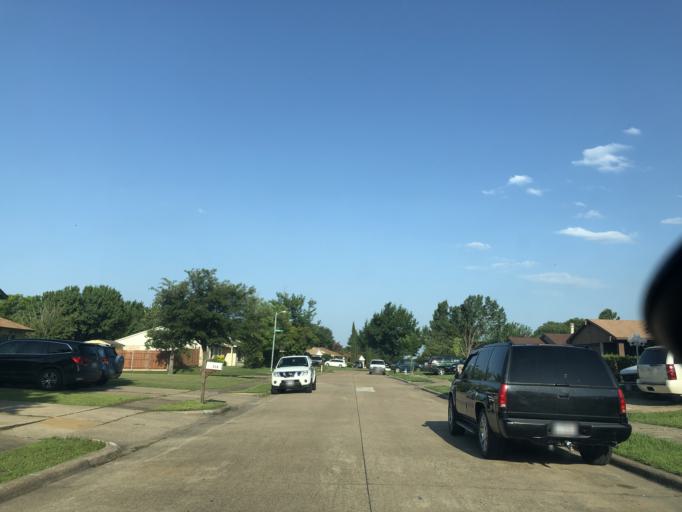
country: US
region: Texas
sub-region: Dallas County
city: Sunnyvale
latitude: 32.8158
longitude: -96.5999
